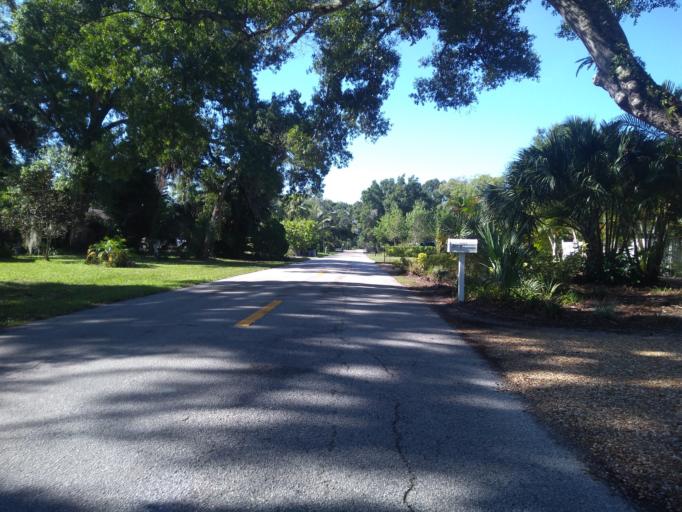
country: US
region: Florida
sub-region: Indian River County
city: Vero Beach
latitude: 27.6328
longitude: -80.4122
